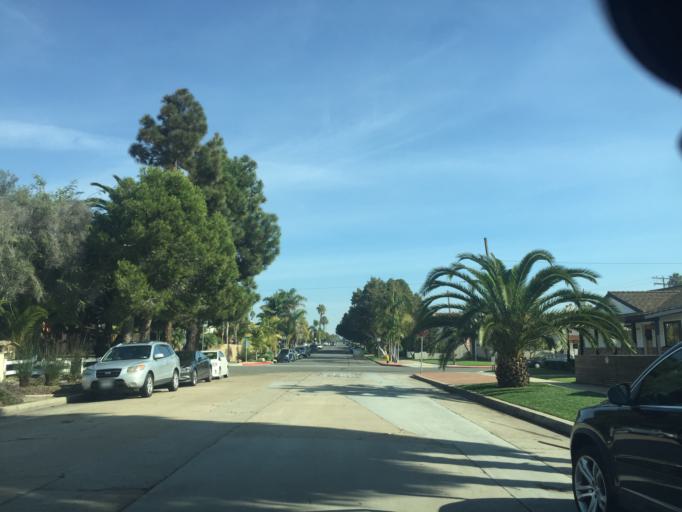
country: US
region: California
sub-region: San Diego County
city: La Jolla
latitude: 32.7929
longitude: -117.2491
